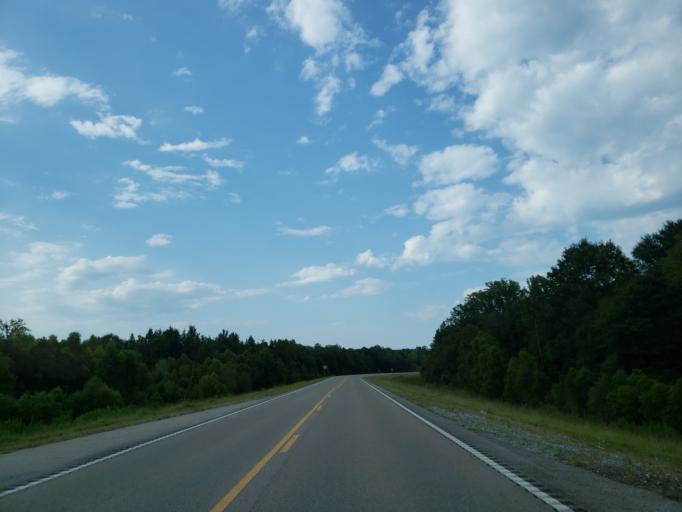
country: US
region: Mississippi
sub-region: Clarke County
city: Stonewall
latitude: 32.1733
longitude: -88.9295
